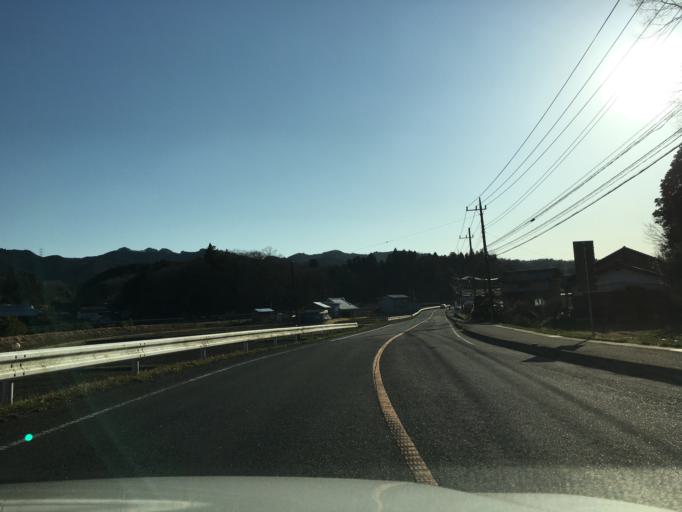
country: JP
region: Ibaraki
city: Daigo
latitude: 36.7792
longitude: 140.3060
